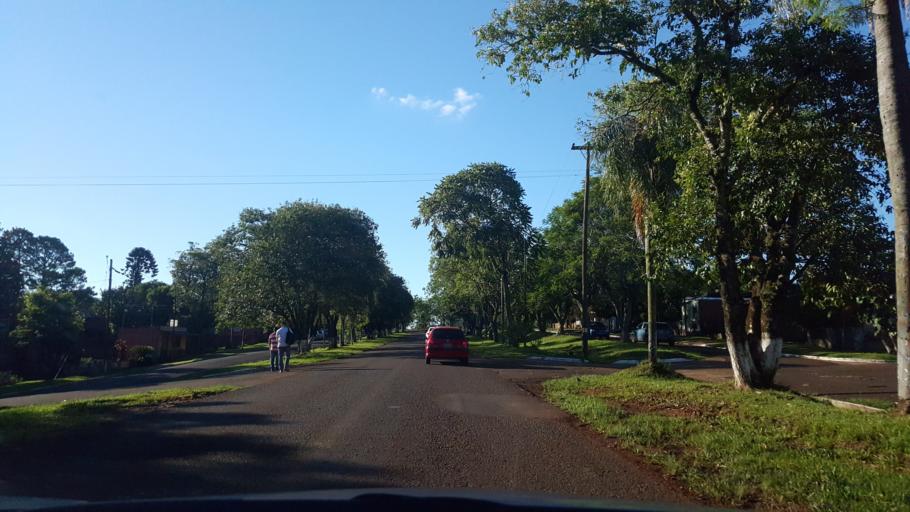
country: AR
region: Misiones
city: Gobernador Roca
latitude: -27.1313
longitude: -55.5088
